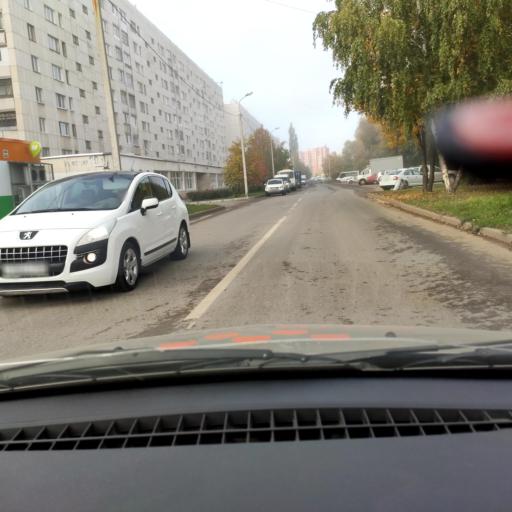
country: RU
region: Bashkortostan
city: Ufa
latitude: 54.7795
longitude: 56.1310
